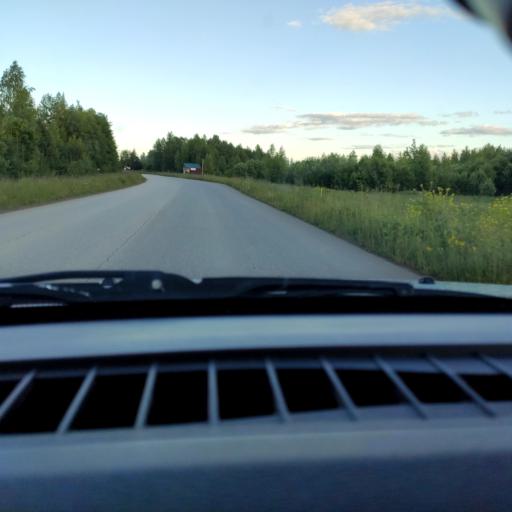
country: RU
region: Perm
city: Polazna
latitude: 58.2049
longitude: 56.4675
